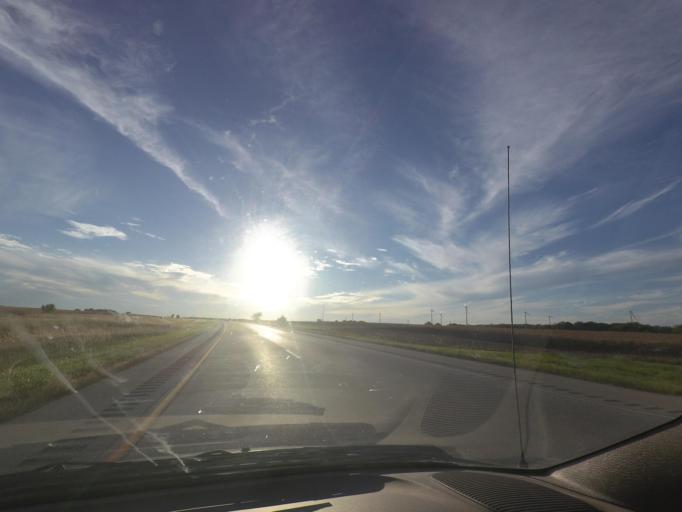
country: US
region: Illinois
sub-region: Sangamon County
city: New Berlin
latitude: 39.7397
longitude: -89.9740
